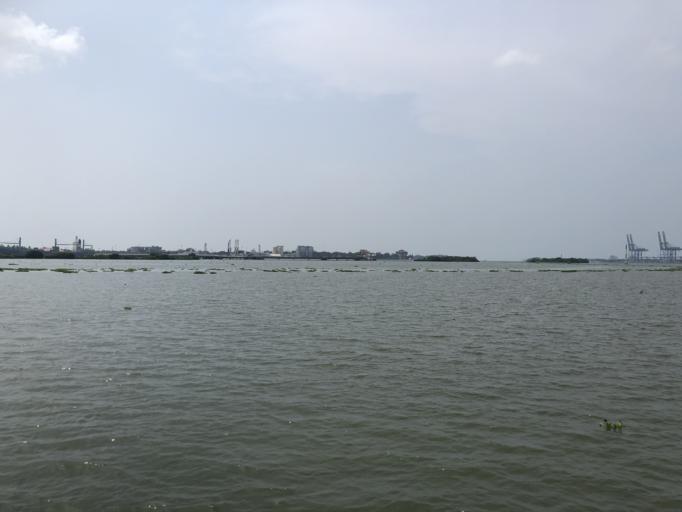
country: IN
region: Kerala
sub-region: Ernakulam
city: Cochin
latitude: 9.9761
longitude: 76.2761
